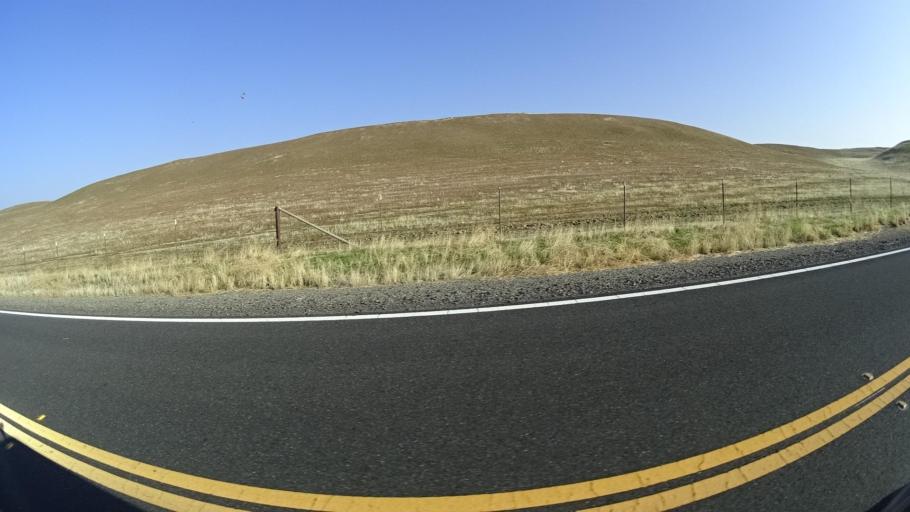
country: US
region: California
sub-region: Tulare County
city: Richgrove
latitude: 35.7456
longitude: -118.9645
